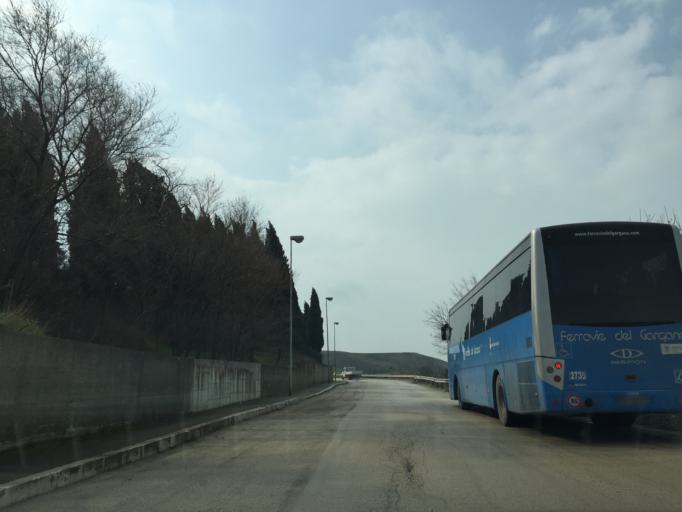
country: IT
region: Apulia
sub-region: Provincia di Foggia
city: Troia
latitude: 41.3600
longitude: 15.3028
